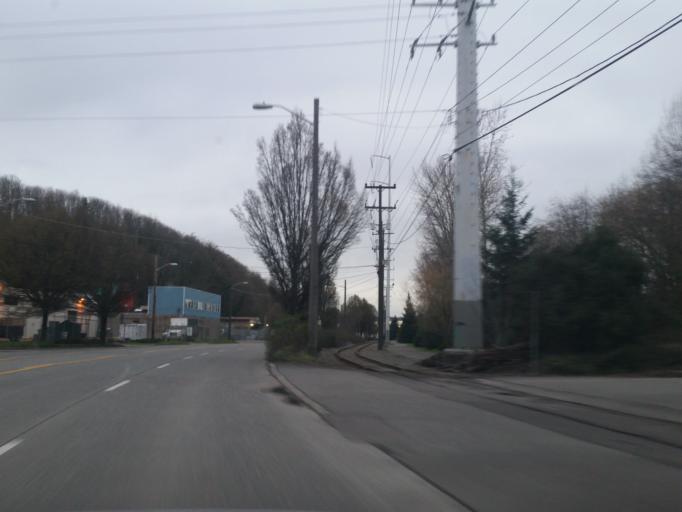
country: US
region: Washington
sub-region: King County
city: White Center
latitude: 47.5575
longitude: -122.3515
